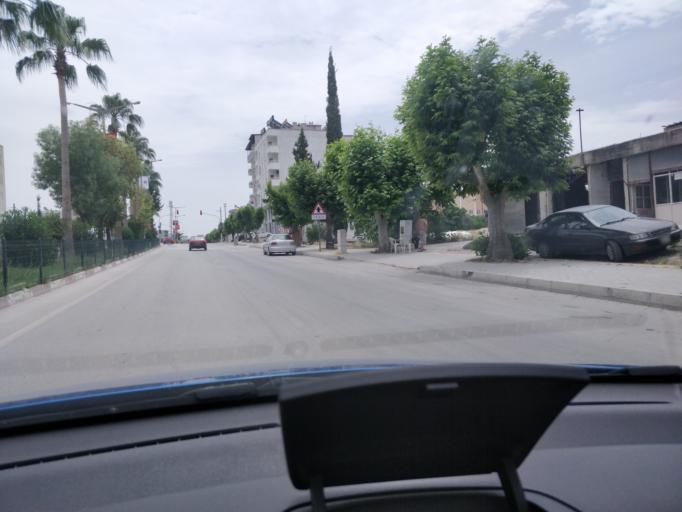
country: TR
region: Mersin
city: Mut
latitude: 36.6386
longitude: 33.4437
